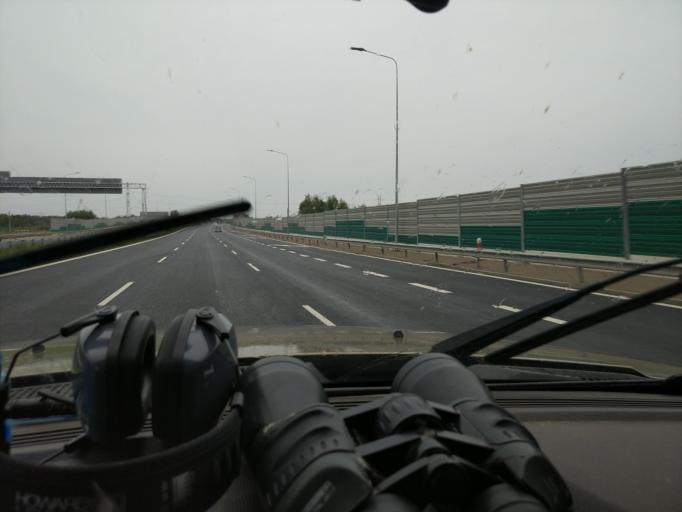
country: PL
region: Masovian Voivodeship
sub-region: Powiat wolominski
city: Radzymin
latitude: 52.4015
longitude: 21.2019
